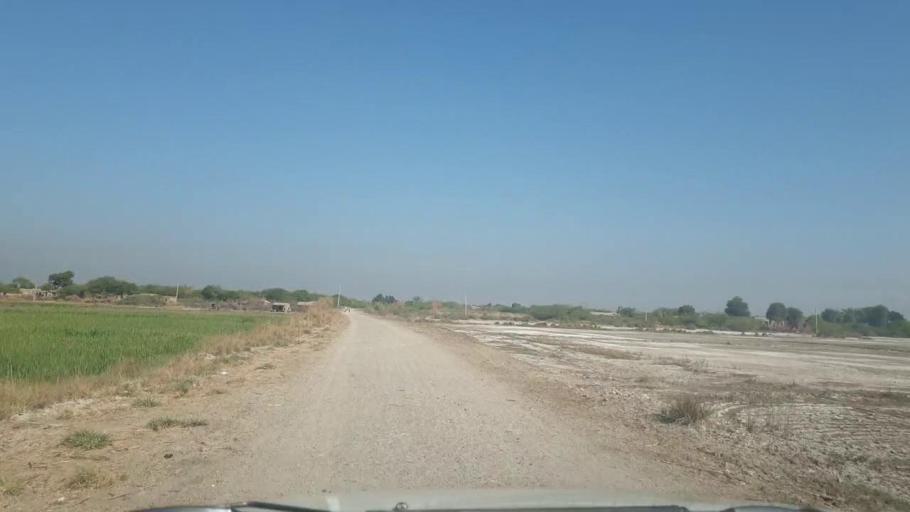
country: PK
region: Sindh
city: Mirpur Khas
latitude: 25.5137
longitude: 69.1494
